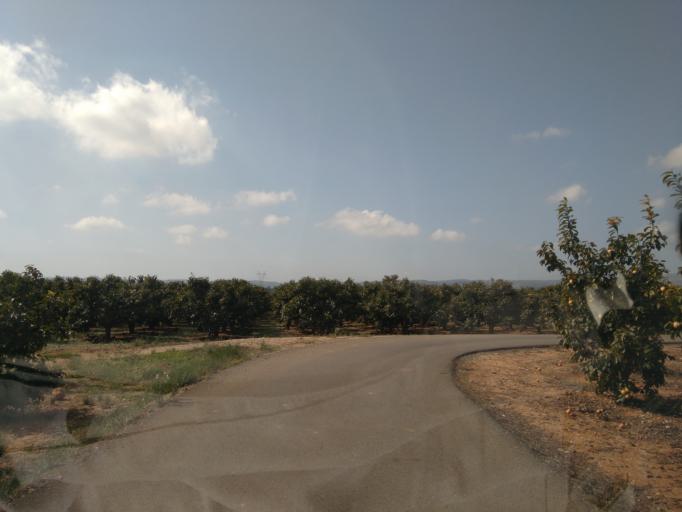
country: ES
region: Valencia
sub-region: Provincia de Valencia
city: Benimodo
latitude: 39.1830
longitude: -0.5432
